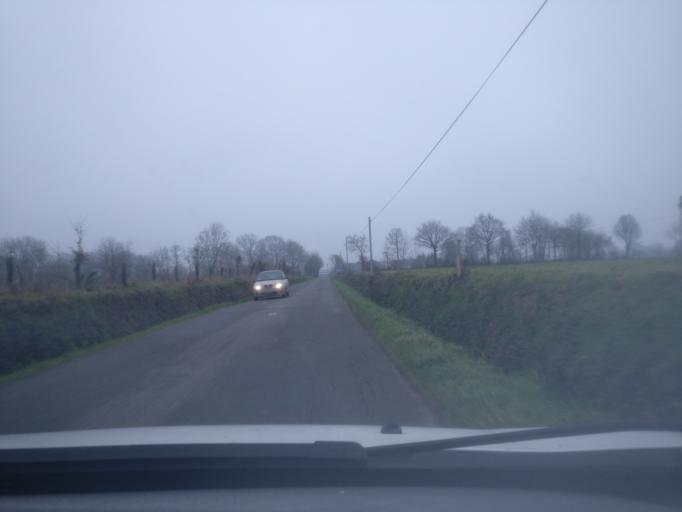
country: FR
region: Brittany
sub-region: Departement d'Ille-et-Vilaine
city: Montreuil-sur-Ille
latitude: 48.3193
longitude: -1.6364
